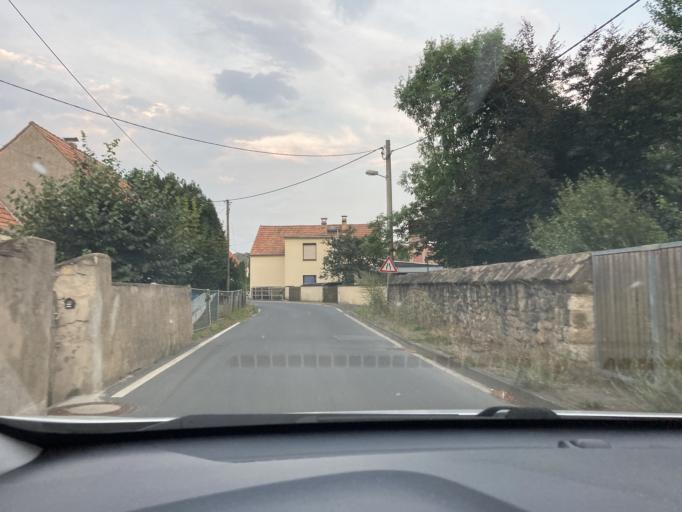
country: DE
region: Saxony
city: Niederau
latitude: 51.1858
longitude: 13.5547
